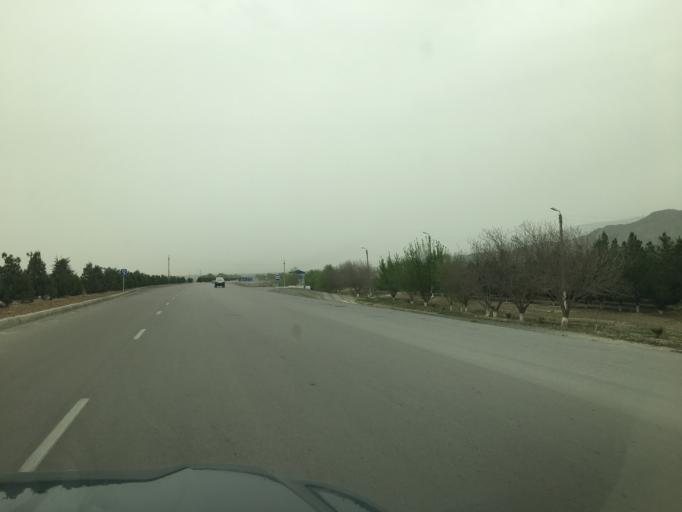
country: TM
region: Ahal
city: Baharly
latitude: 38.2688
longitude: 57.7081
